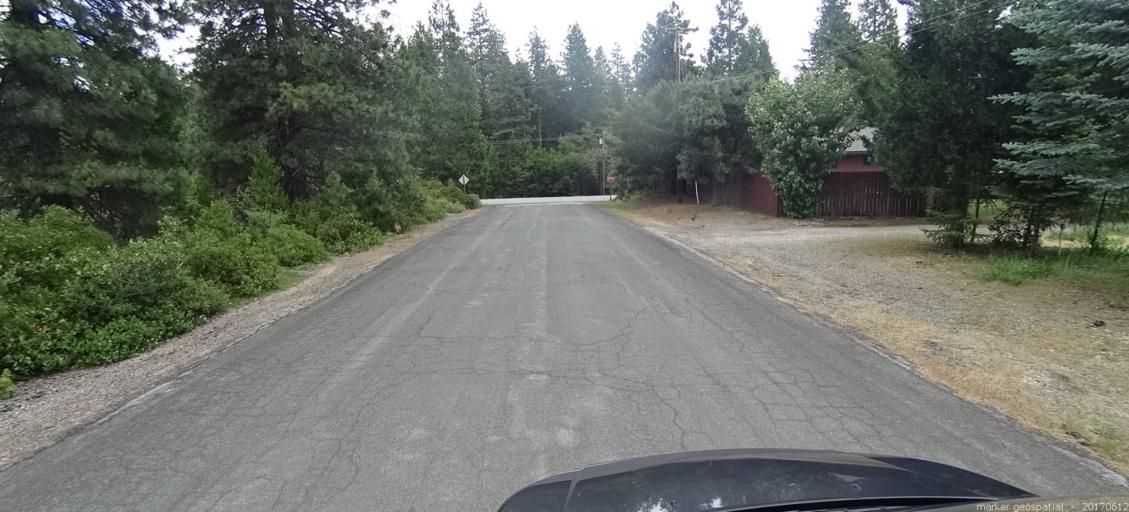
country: US
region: California
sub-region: Siskiyou County
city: Mount Shasta
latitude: 41.3440
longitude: -122.3577
